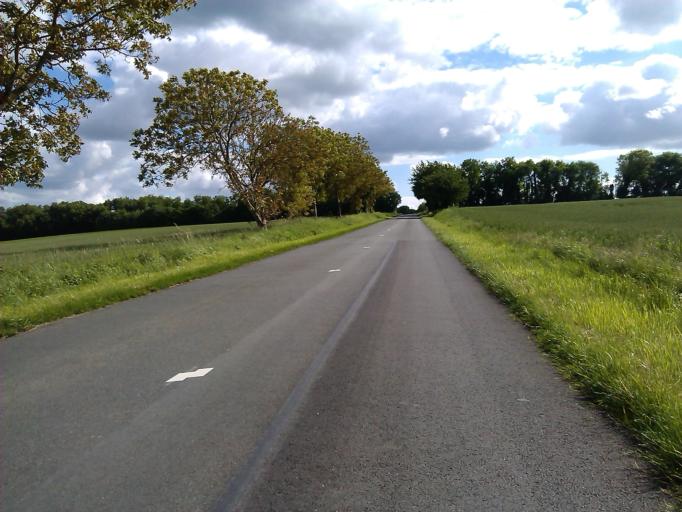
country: FR
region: Poitou-Charentes
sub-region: Departement de la Charente
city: Mansle
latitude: 45.8566
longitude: 0.1644
